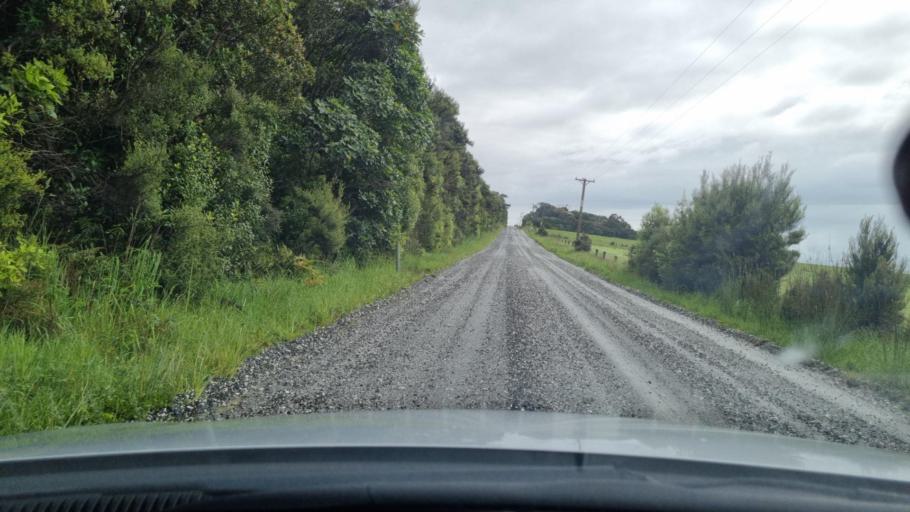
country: NZ
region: Southland
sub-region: Invercargill City
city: Bluff
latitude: -46.5311
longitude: 168.2679
